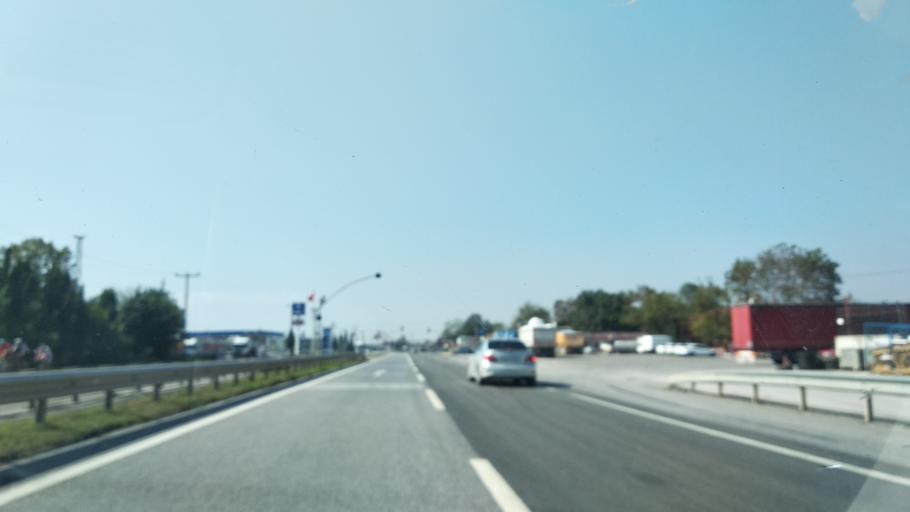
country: TR
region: Kocaeli
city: Derbent
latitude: 40.7295
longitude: 30.1456
